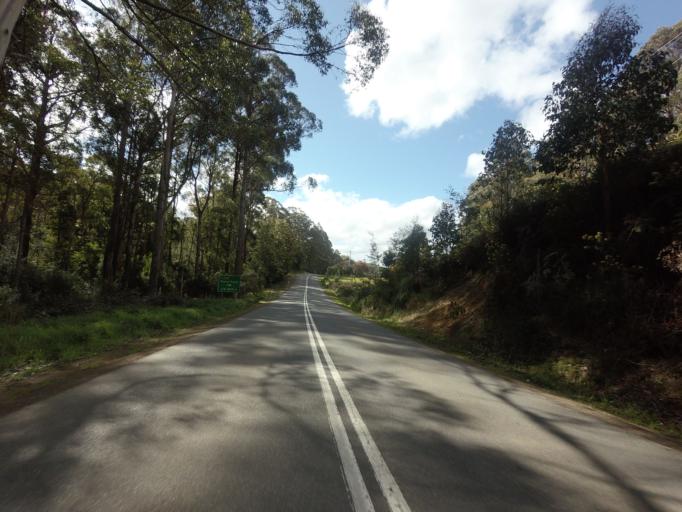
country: AU
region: Tasmania
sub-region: Huon Valley
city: Geeveston
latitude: -43.2215
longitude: 146.9878
